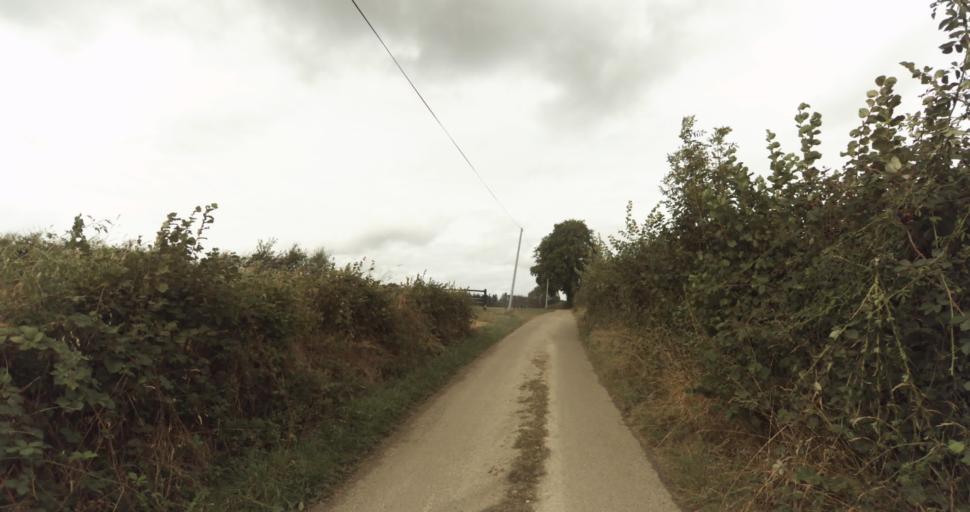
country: FR
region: Lower Normandy
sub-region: Departement de l'Orne
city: Gace
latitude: 48.8247
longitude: 0.3631
